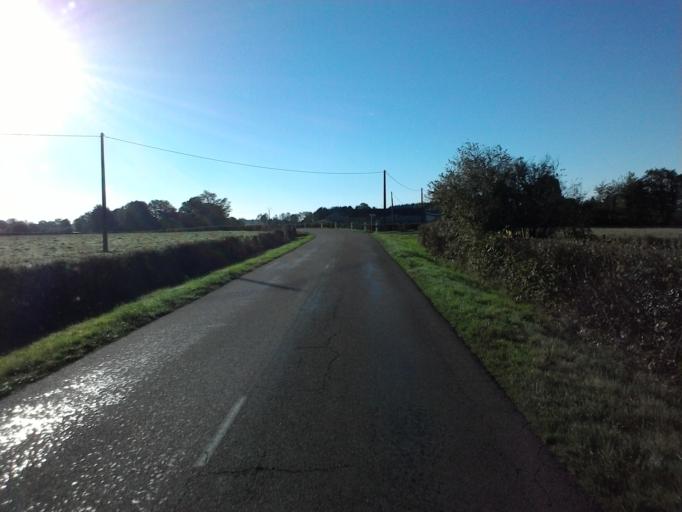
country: FR
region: Bourgogne
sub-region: Departement de la Cote-d'Or
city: Saulieu
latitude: 47.2793
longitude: 4.1928
